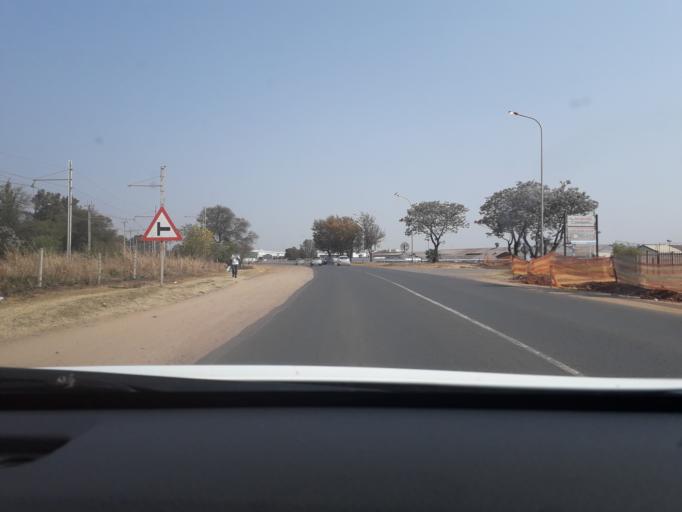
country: ZA
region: Gauteng
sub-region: Ekurhuleni Metropolitan Municipality
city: Tembisa
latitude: -25.9585
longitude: 28.2317
